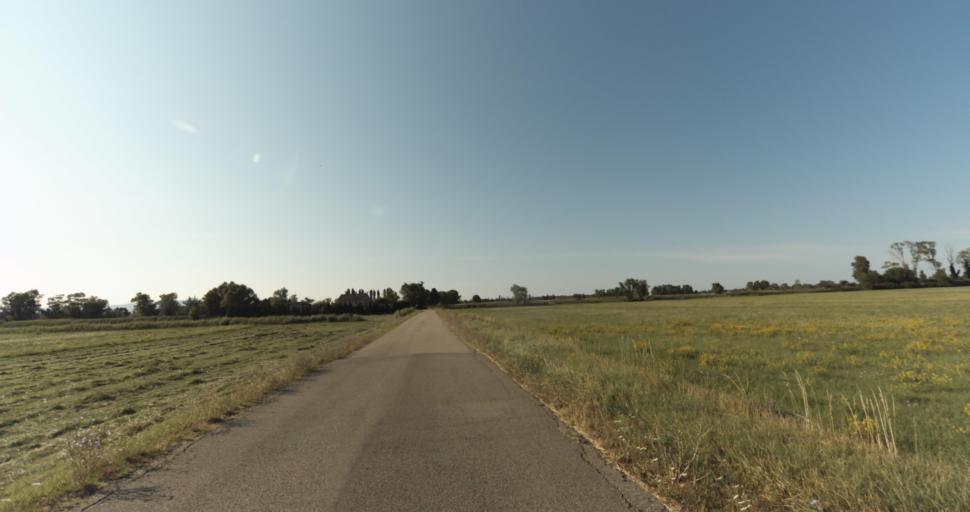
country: FR
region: Provence-Alpes-Cote d'Azur
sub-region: Departement du Vaucluse
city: Sarrians
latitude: 44.0494
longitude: 4.9509
